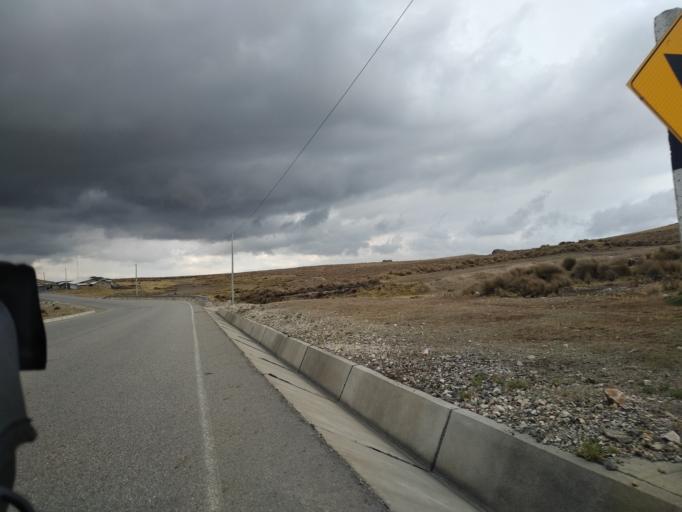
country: PE
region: La Libertad
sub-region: Provincia de Santiago de Chuco
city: Quiruvilca
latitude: -7.9903
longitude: -78.2887
